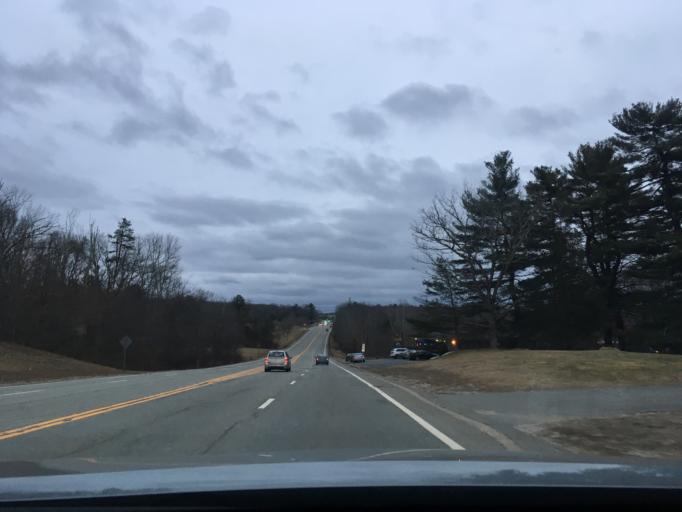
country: US
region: Rhode Island
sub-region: Providence County
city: Smithfield
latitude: 41.9249
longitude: -71.5316
